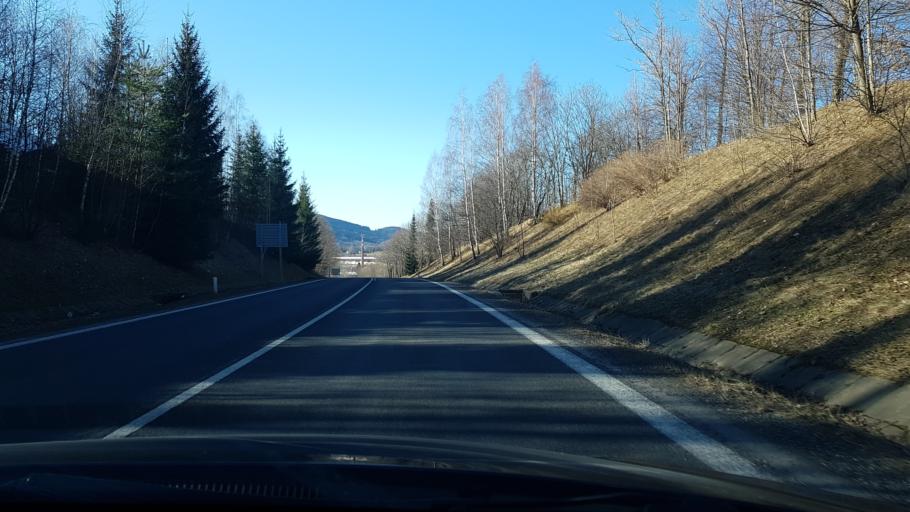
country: CZ
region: Olomoucky
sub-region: Okres Jesenik
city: Jesenik
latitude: 50.2183
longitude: 17.1973
